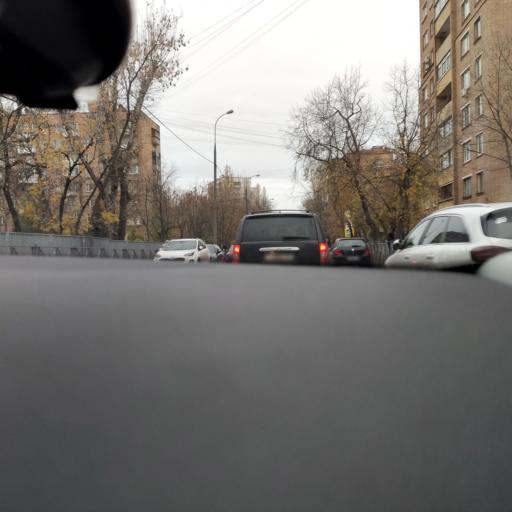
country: RU
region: Moscow
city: Tekstil'shchiki
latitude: 55.7011
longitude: 37.7423
